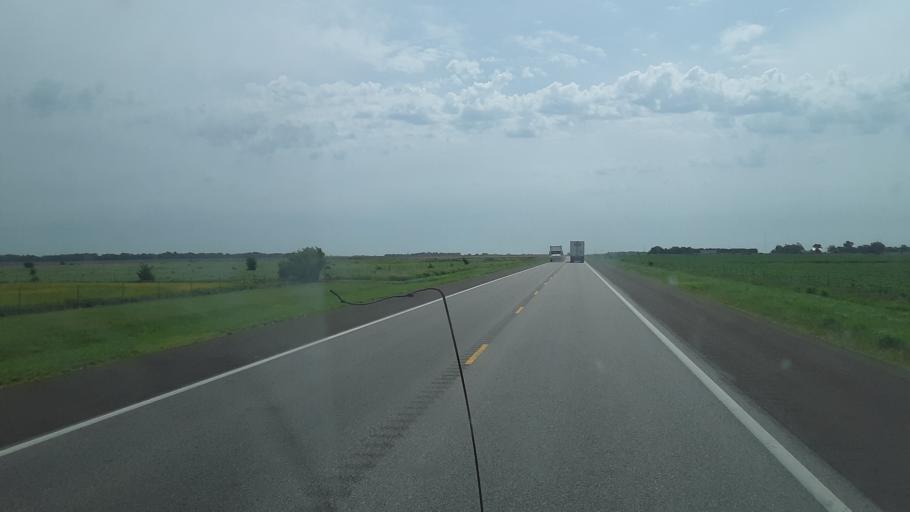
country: US
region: Kansas
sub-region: Reno County
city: Nickerson
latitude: 37.9849
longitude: -98.1204
